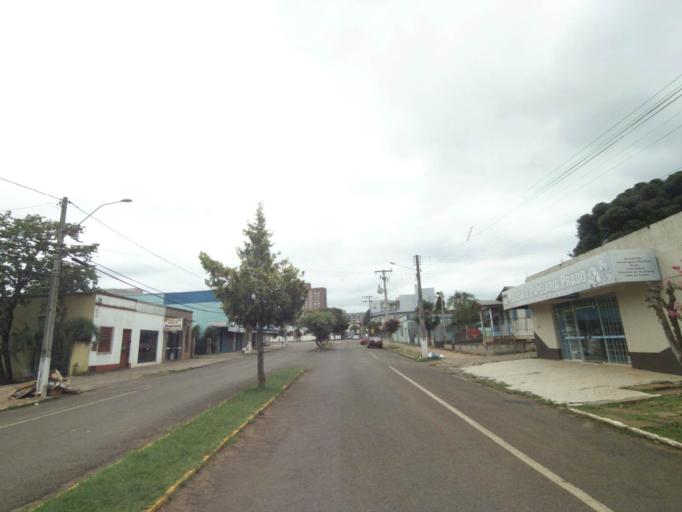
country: BR
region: Rio Grande do Sul
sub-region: Lagoa Vermelha
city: Lagoa Vermelha
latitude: -28.2096
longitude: -51.5308
